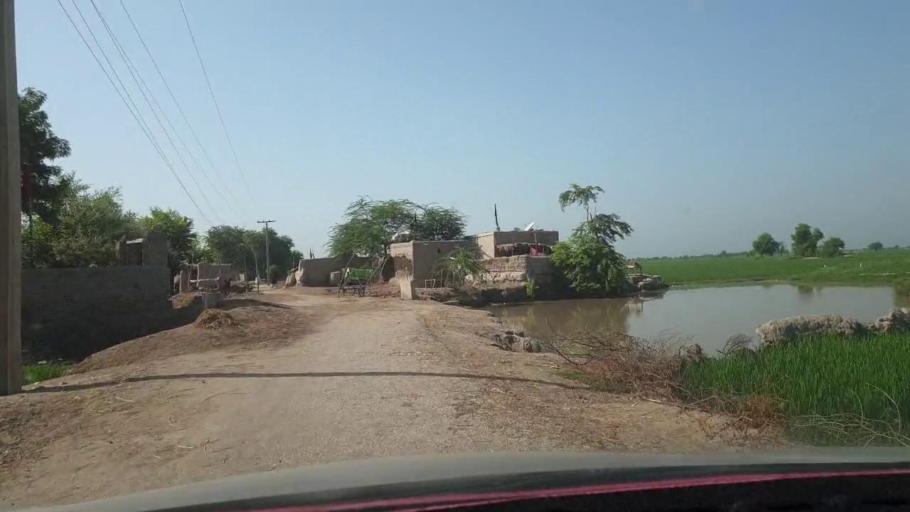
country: PK
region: Sindh
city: Nasirabad
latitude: 27.3806
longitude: 67.8818
